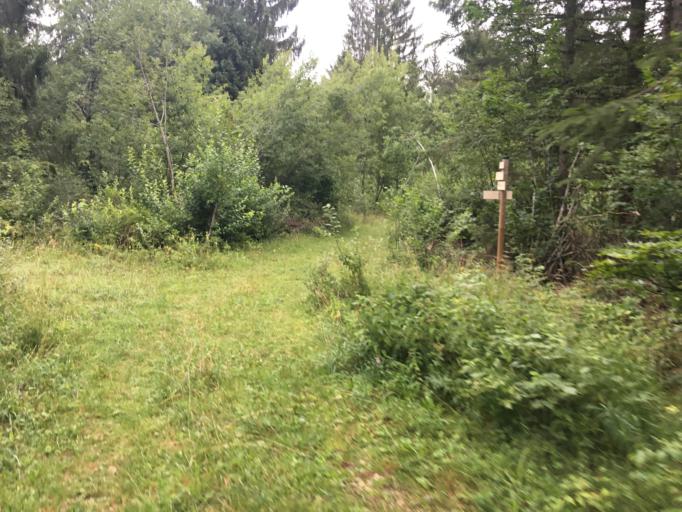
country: FR
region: Franche-Comte
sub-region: Departement du Jura
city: Morbier
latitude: 46.6091
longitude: 5.9807
